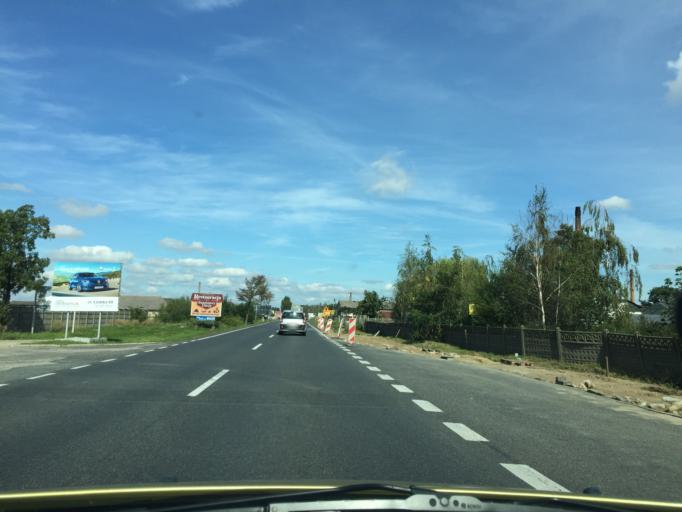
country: PL
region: Greater Poland Voivodeship
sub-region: Kalisz
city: Kalisz
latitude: 51.7959
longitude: 18.0916
